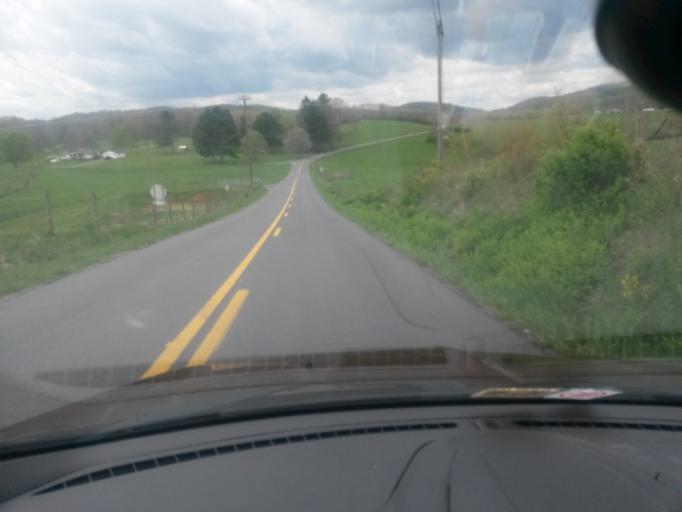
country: US
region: West Virginia
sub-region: Greenbrier County
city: Lewisburg
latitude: 37.9271
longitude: -80.3877
